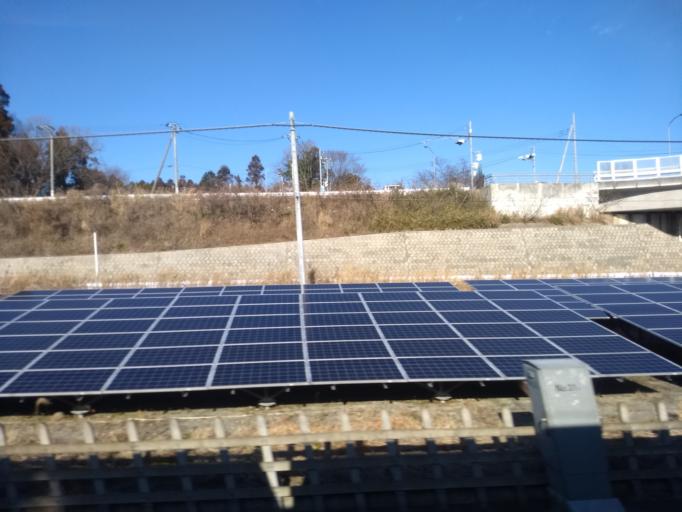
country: JP
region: Chiba
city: Sakura
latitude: 35.7887
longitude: 140.1999
